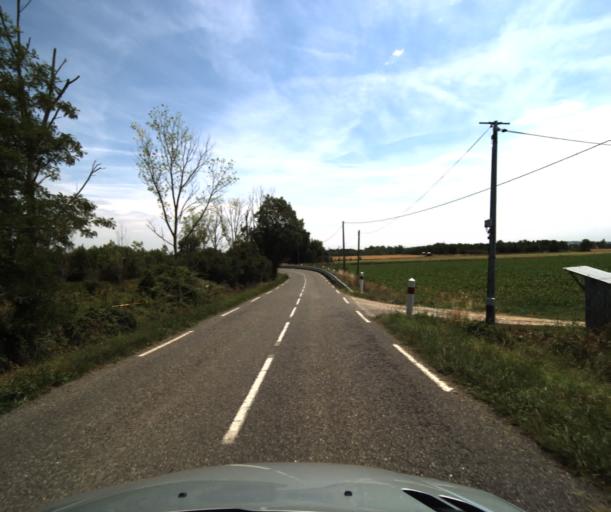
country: FR
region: Midi-Pyrenees
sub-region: Departement de la Haute-Garonne
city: Labastidette
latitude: 43.4515
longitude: 1.2332
